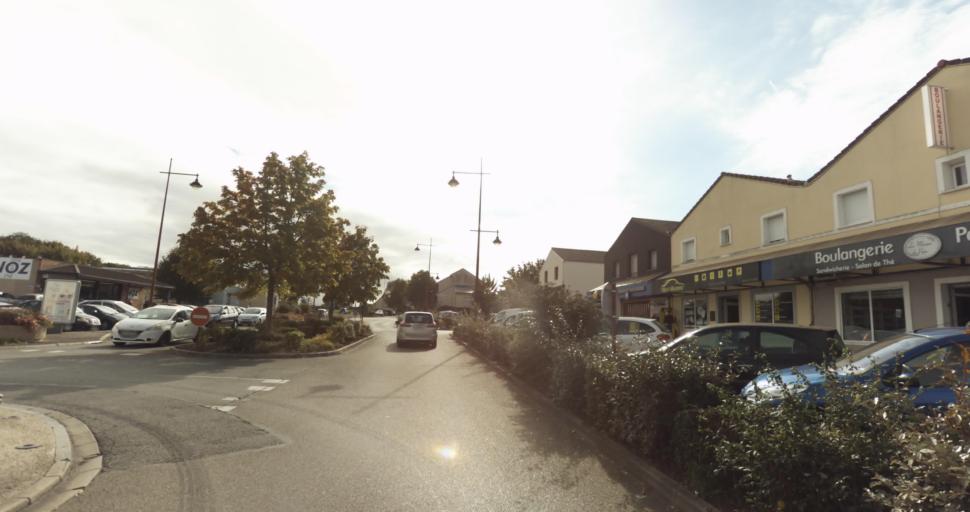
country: FR
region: Centre
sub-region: Departement d'Eure-et-Loir
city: Garnay
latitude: 48.7301
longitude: 1.3402
